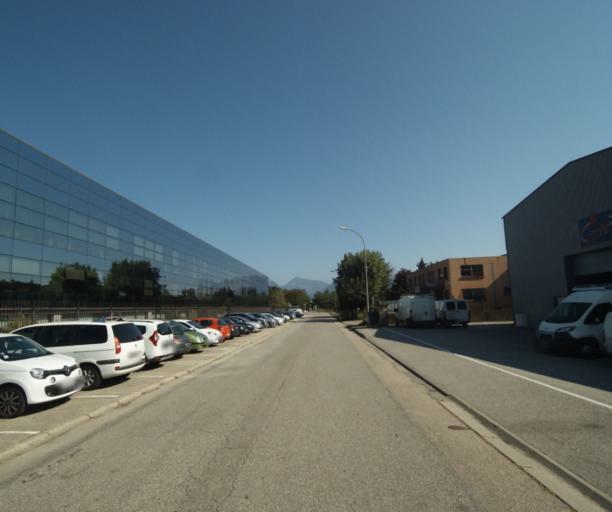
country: FR
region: Rhone-Alpes
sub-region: Departement de l'Isere
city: Le Pont-de-Claix
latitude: 45.1374
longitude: 5.6939
